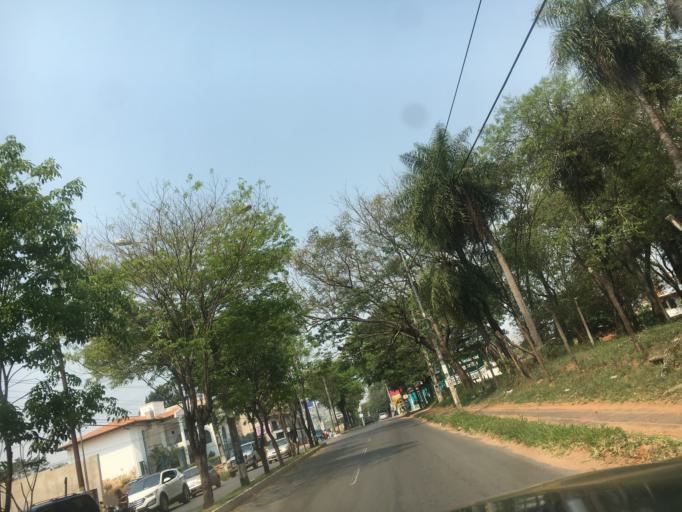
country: PY
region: Central
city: Villa Elisa
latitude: -25.3666
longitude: -57.5880
